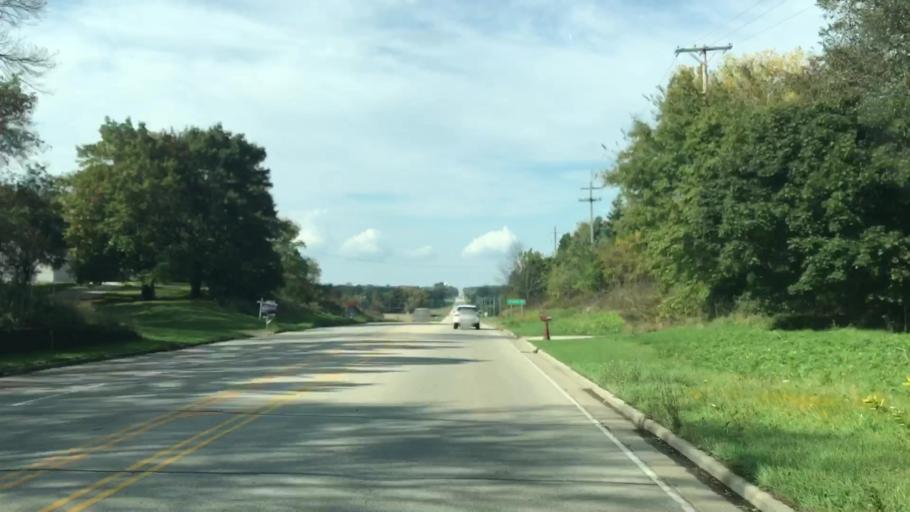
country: US
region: Wisconsin
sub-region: Ozaukee County
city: Mequon
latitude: 43.2216
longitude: -88.0206
